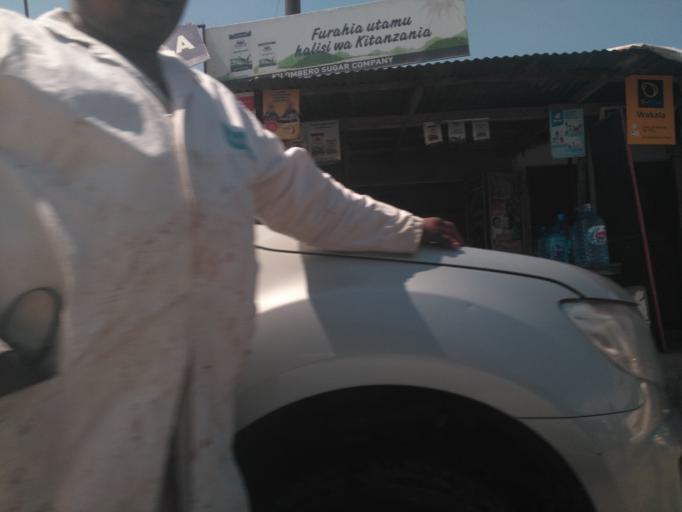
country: TZ
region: Dar es Salaam
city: Magomeni
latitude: -6.7885
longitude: 39.2645
